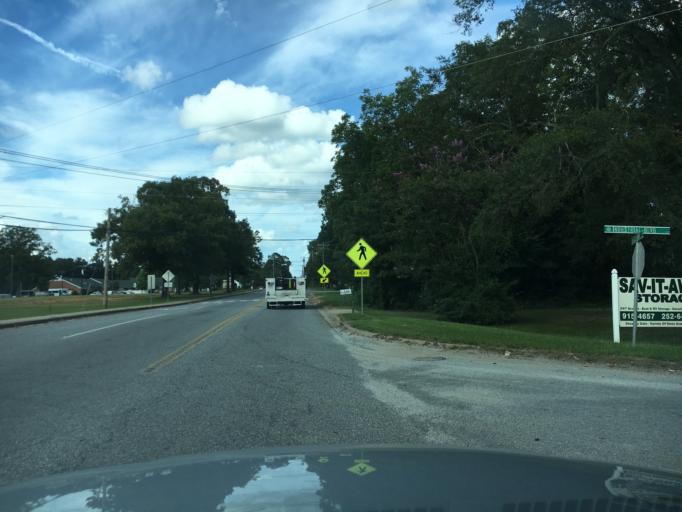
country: US
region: South Carolina
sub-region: Greenville County
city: Fountain Inn
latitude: 34.6936
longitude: -82.1923
